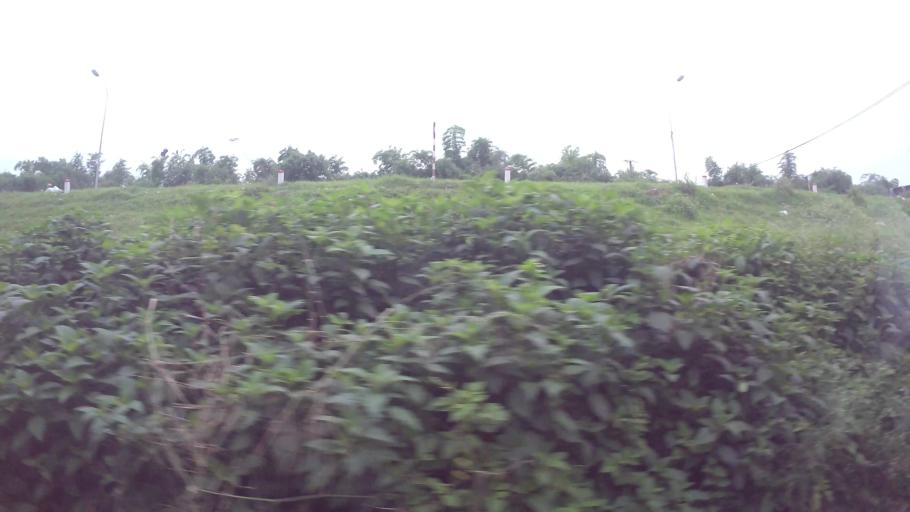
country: VN
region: Ha Noi
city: Trau Quy
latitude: 21.0467
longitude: 105.9285
